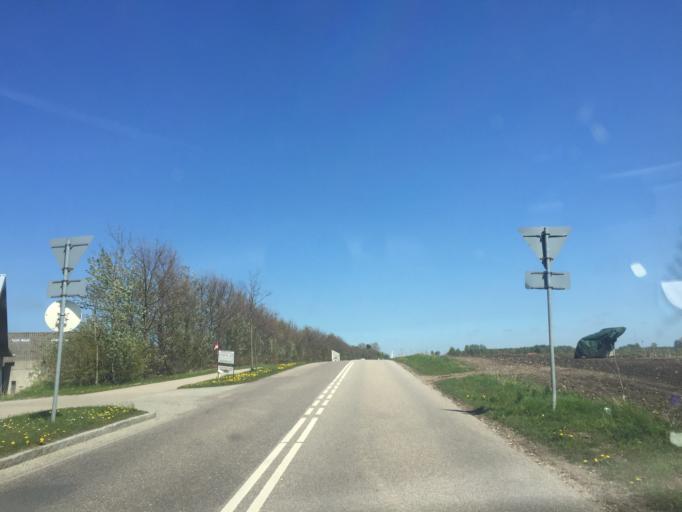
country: DK
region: Capital Region
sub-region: Egedal Kommune
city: Vekso
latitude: 55.7758
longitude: 12.2358
